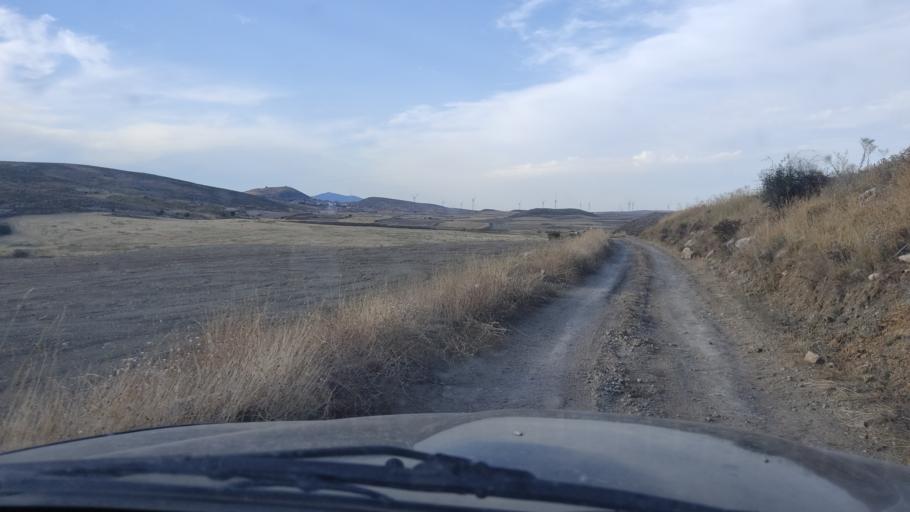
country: ES
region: Aragon
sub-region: Provincia de Teruel
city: Monforte de Moyuela
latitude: 41.0343
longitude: -0.9978
